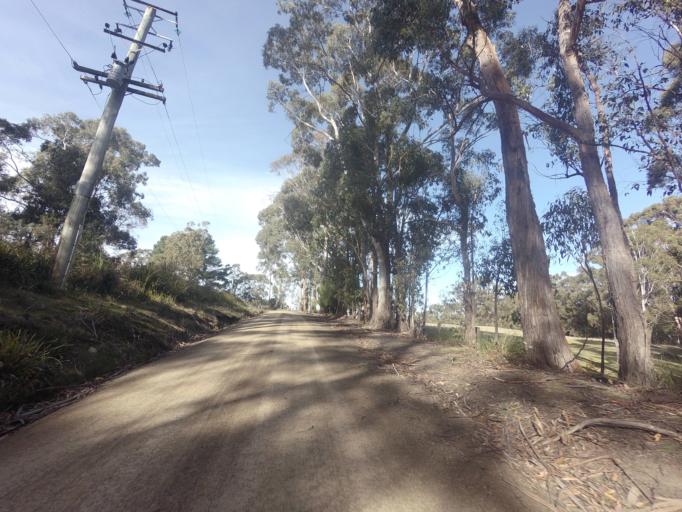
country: AU
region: Tasmania
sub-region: Kingborough
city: Kettering
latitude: -43.1009
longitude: 147.2619
